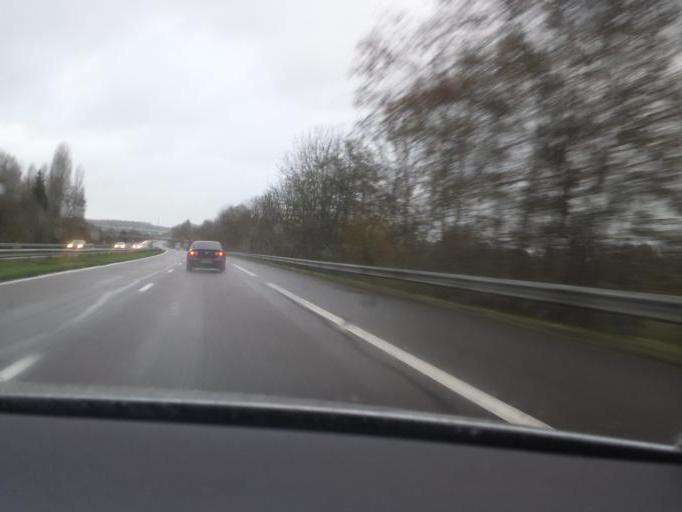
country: FR
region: Haute-Normandie
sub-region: Departement de l'Eure
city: Pacy-sur-Eure
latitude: 49.0076
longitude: 1.3754
